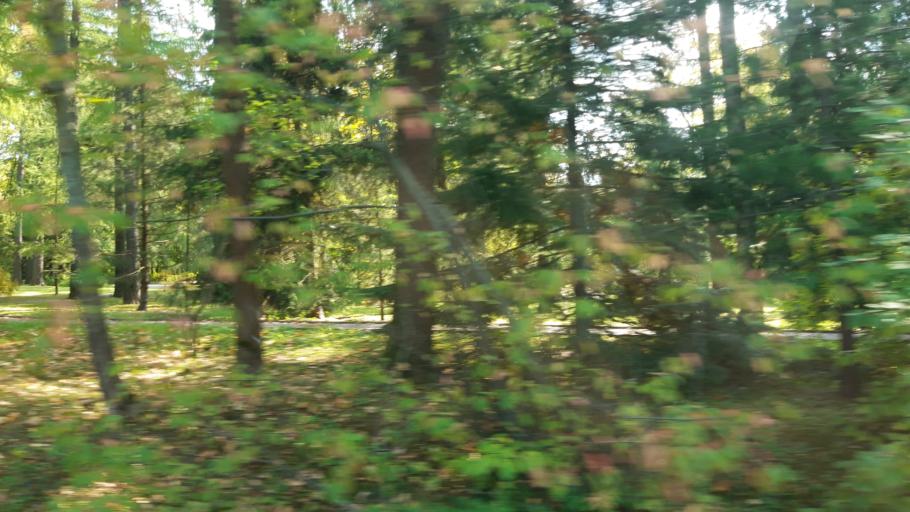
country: RU
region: Moskovskaya
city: Mendeleyevo
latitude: 56.0517
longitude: 37.2206
